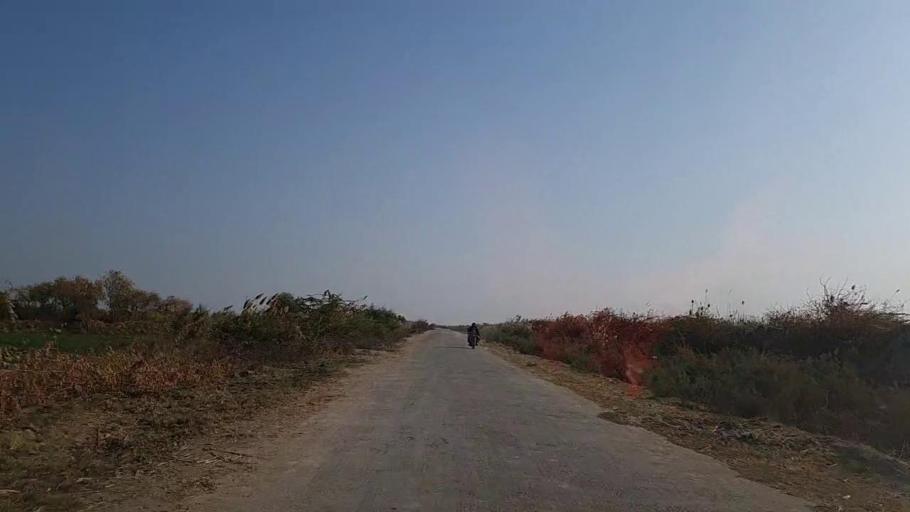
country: PK
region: Sindh
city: Tando Mittha Khan
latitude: 25.9220
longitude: 69.0693
